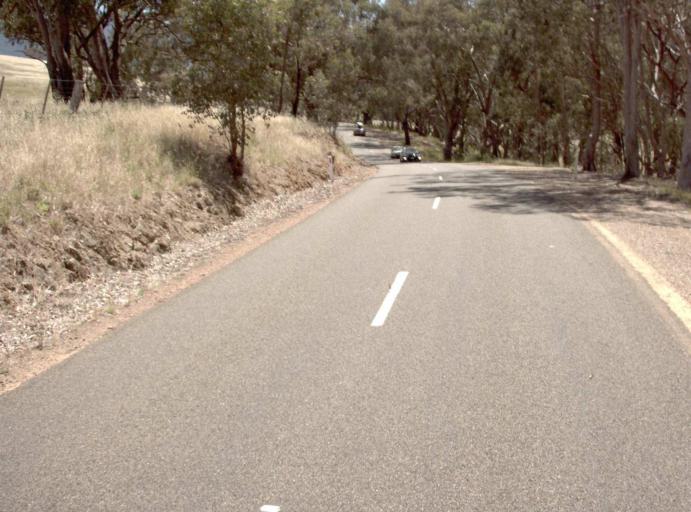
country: AU
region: Victoria
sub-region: East Gippsland
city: Bairnsdale
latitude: -37.2171
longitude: 147.7161
